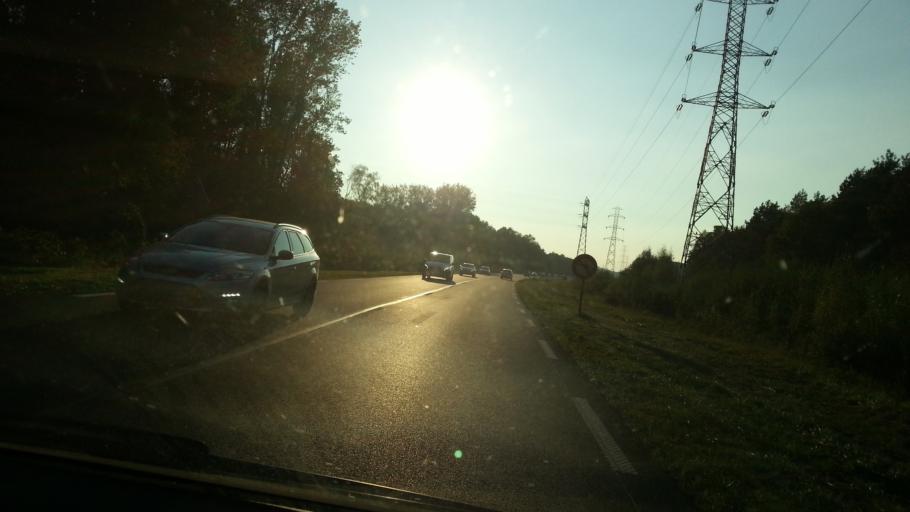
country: FR
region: Picardie
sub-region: Departement de l'Oise
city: Les Ageux
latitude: 49.3201
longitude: 2.5909
